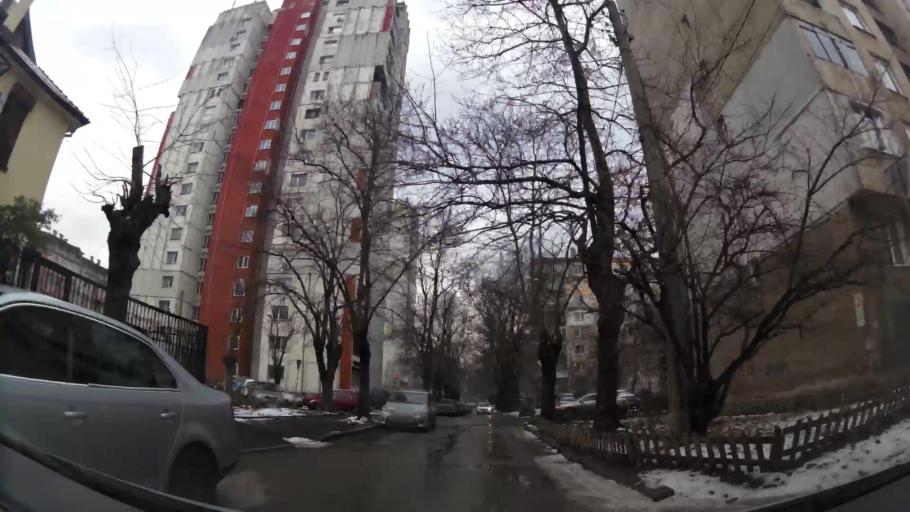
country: BG
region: Sofia-Capital
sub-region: Stolichna Obshtina
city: Sofia
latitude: 42.6876
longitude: 23.2971
